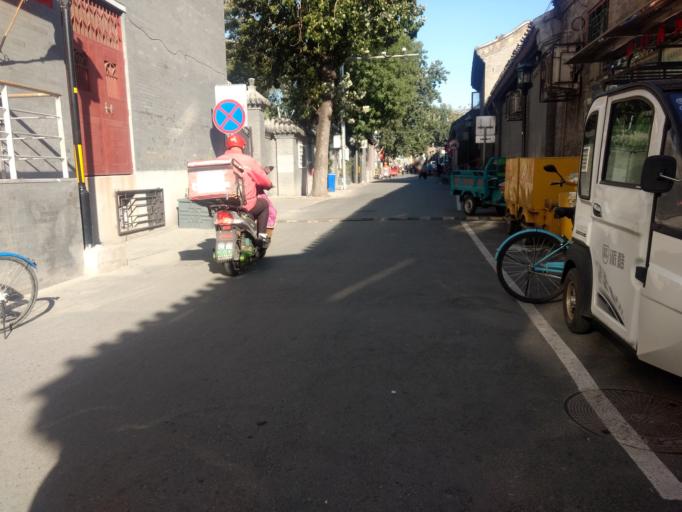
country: CN
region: Beijing
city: Beijing
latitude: 39.8975
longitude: 116.3792
